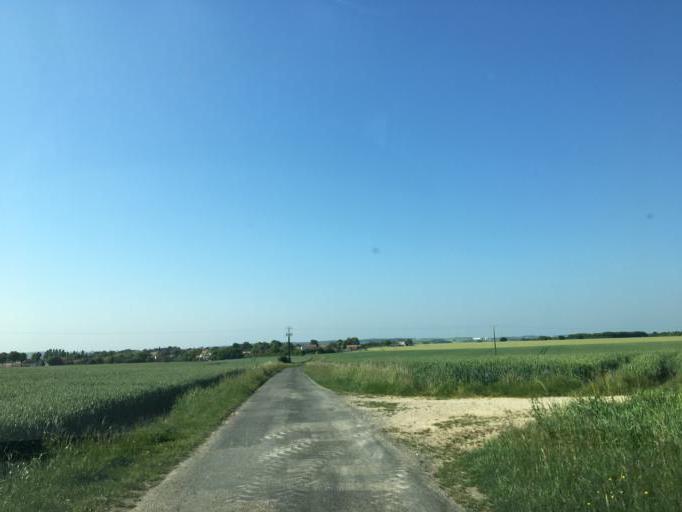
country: FR
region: Poitou-Charentes
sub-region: Departement des Deux-Sevres
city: Beauvoir-sur-Niort
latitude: 46.0820
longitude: -0.5076
